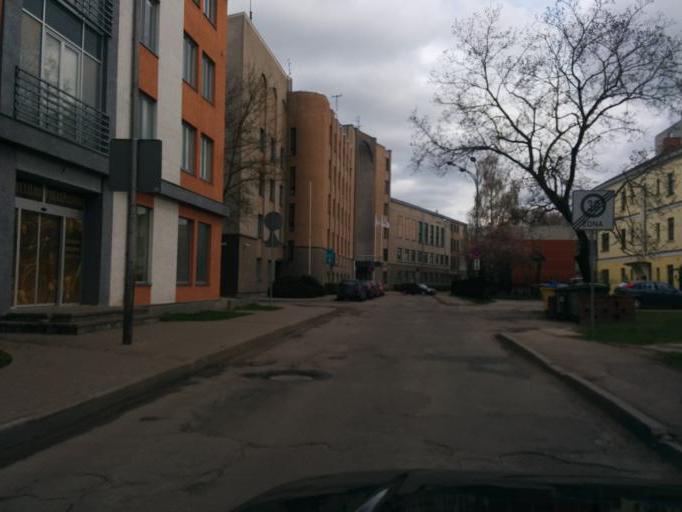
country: LV
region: Jelgava
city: Jelgava
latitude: 56.6494
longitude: 23.7321
